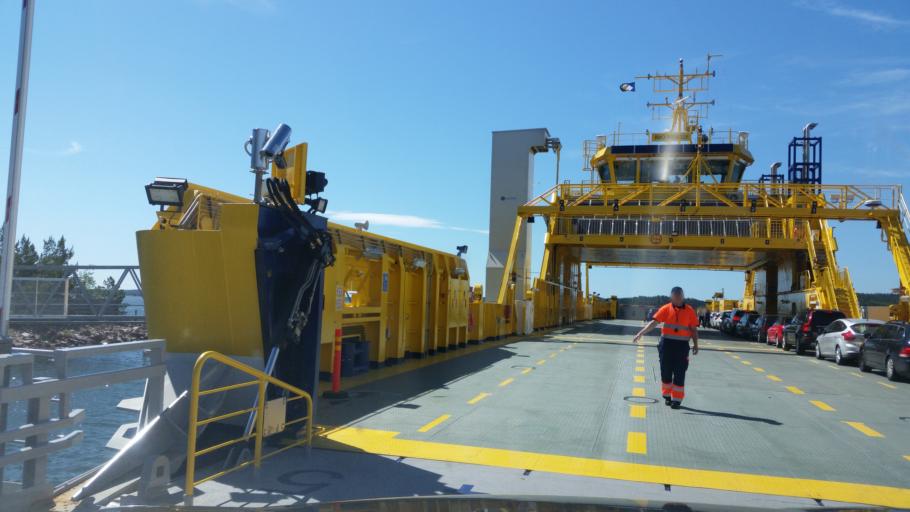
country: FI
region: Varsinais-Suomi
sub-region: Aboland-Turunmaa
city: Laensi-Turunmaa
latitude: 60.2353
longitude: 22.1124
